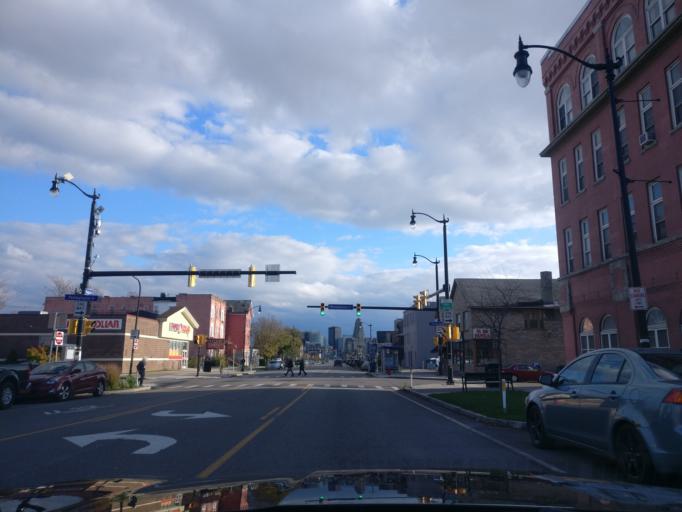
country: US
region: New York
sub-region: Erie County
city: Buffalo
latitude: 42.8984
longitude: -78.8895
